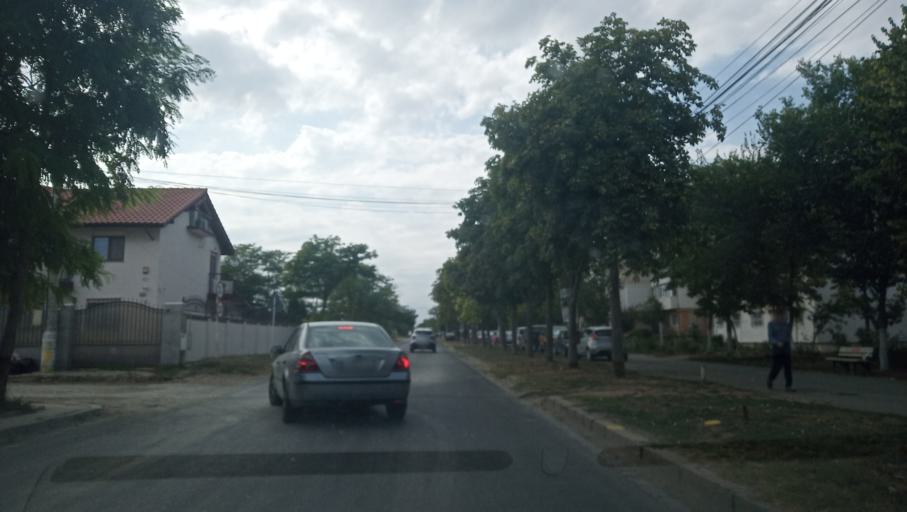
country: RO
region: Constanta
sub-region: Municipiul Mangalia
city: Mangalia
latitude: 43.8143
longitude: 28.5697
